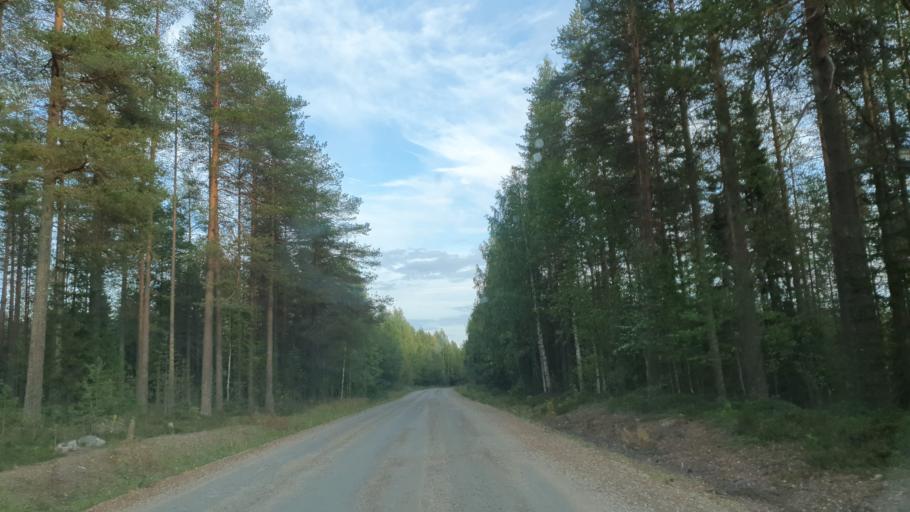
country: FI
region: Kainuu
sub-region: Kehys-Kainuu
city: Kuhmo
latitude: 64.4135
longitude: 29.5288
